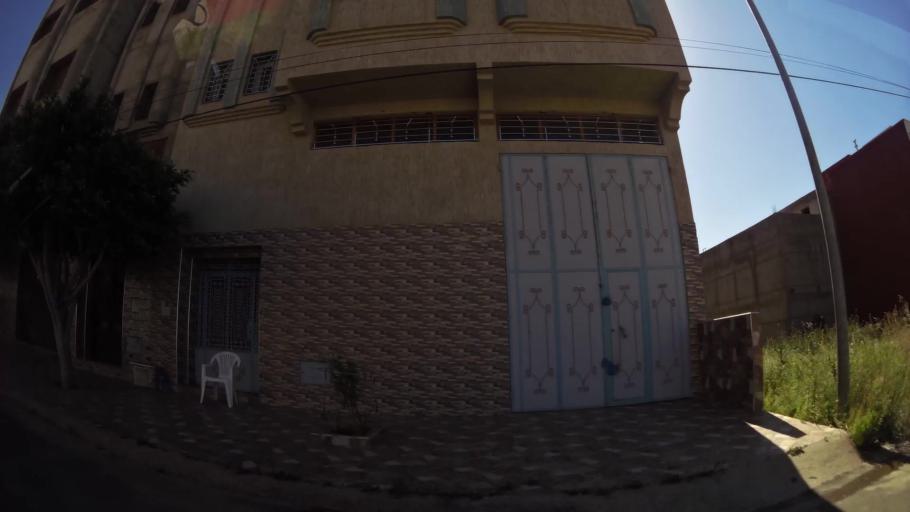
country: MA
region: Oriental
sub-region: Berkane-Taourirt
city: Berkane
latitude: 34.9457
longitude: -2.3344
